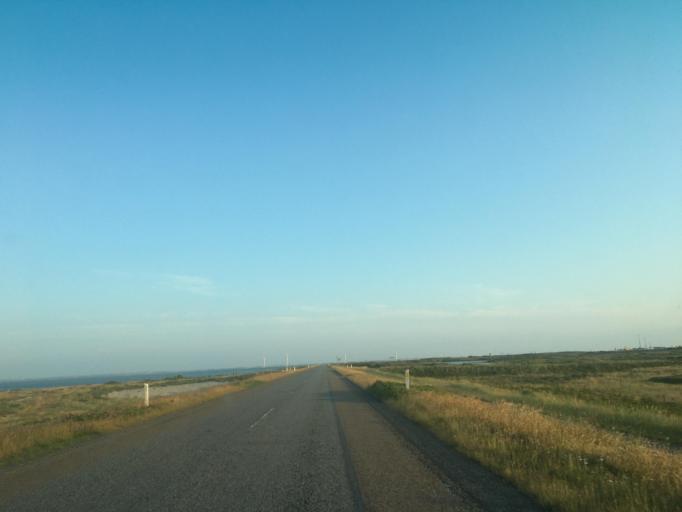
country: DK
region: Central Jutland
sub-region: Lemvig Kommune
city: Thyboron
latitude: 56.7248
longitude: 8.2493
